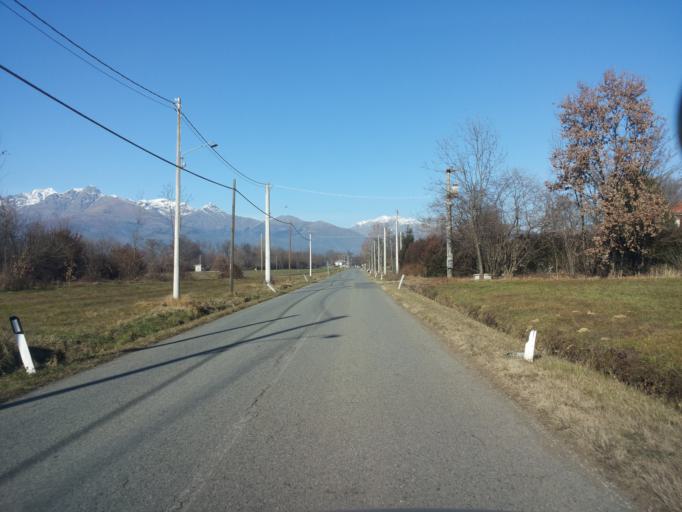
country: IT
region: Piedmont
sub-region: Provincia di Biella
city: Ponderano
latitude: 45.5224
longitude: 8.0529
